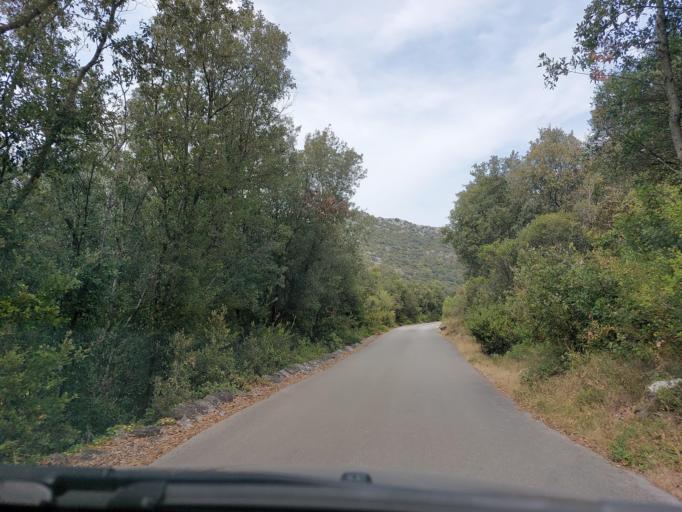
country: HR
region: Dubrovacko-Neretvanska
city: Smokvica
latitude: 42.7633
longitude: 16.9060
